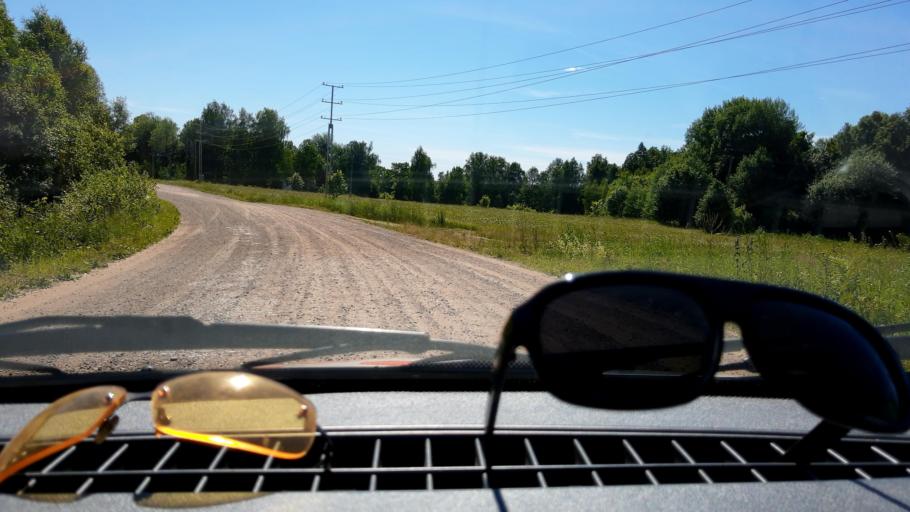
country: RU
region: Bashkortostan
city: Ulu-Telyak
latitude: 54.7827
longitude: 56.9860
